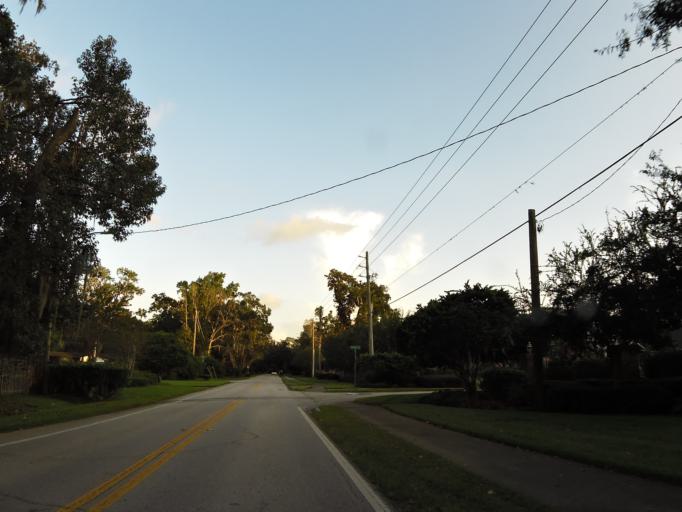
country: US
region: Florida
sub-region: Clay County
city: Orange Park
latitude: 30.1993
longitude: -81.6342
